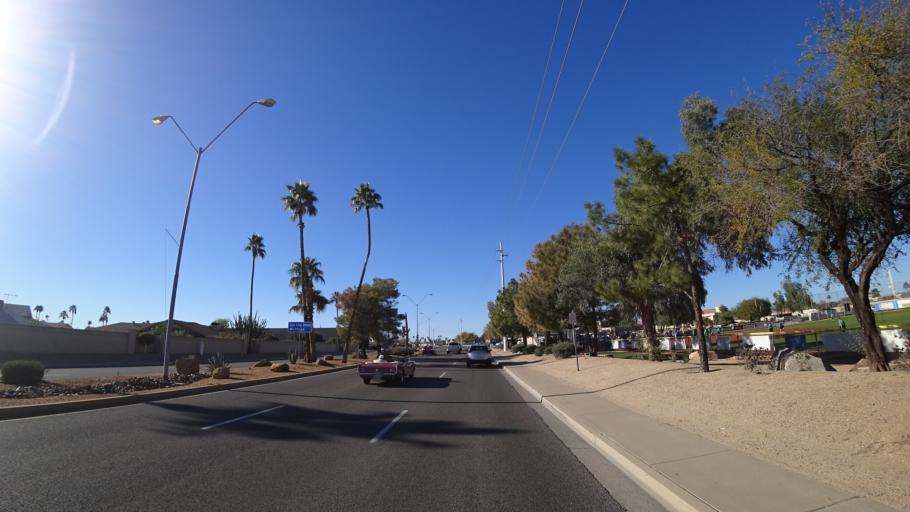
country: US
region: Arizona
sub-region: Maricopa County
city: Sun City West
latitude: 33.6692
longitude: -112.3690
